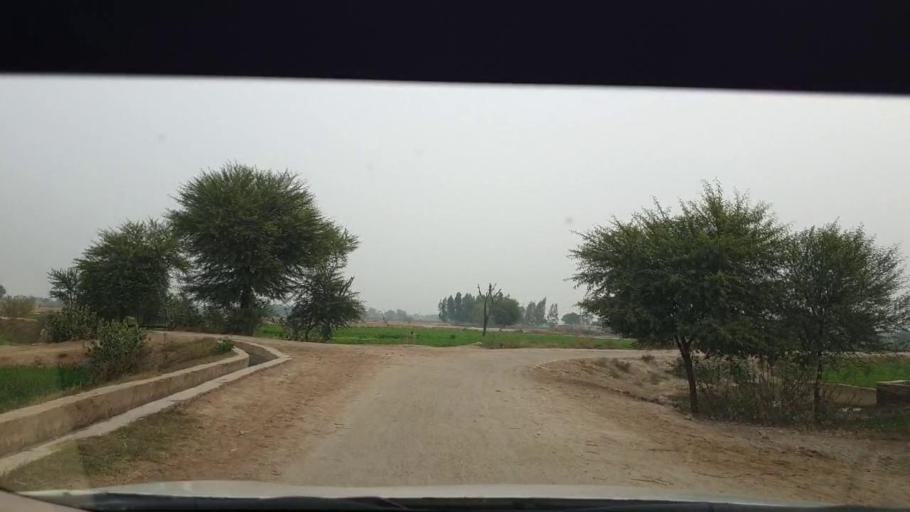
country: PK
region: Sindh
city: Berani
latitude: 25.8748
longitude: 68.8284
